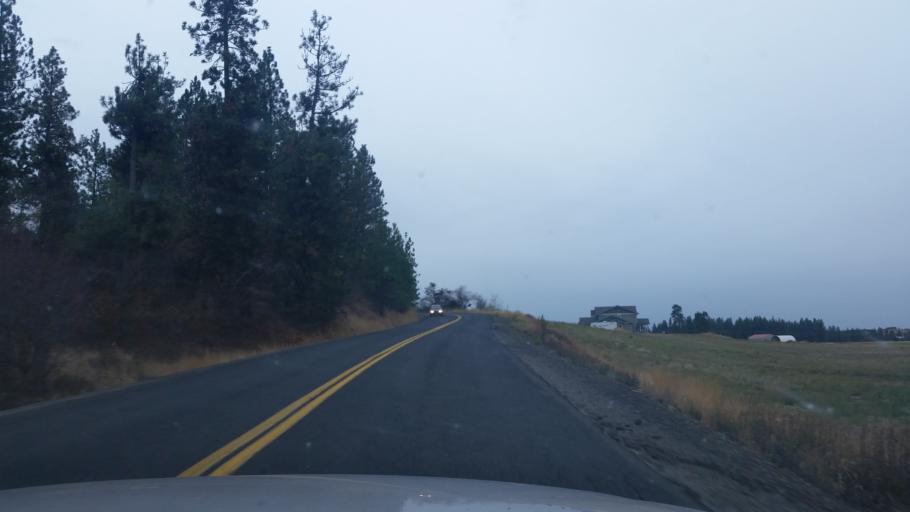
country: US
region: Washington
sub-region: Spokane County
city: Cheney
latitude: 47.5352
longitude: -117.5512
